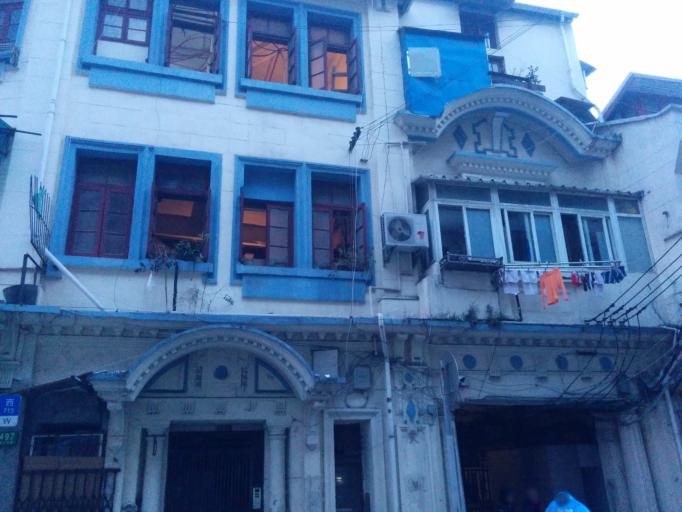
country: CN
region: Shanghai Shi
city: Hongkou
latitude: 31.2397
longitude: 121.4725
